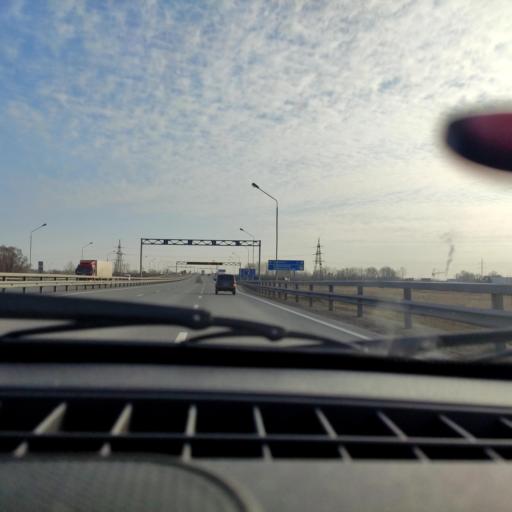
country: RU
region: Bashkortostan
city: Ufa
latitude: 54.6463
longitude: 55.9229
